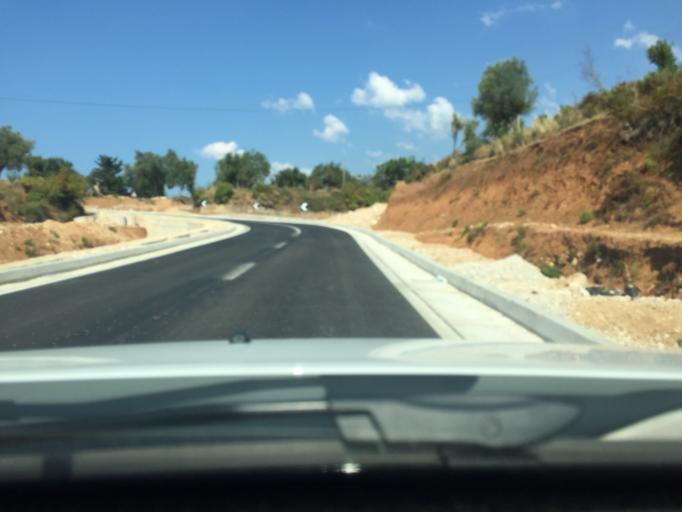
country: AL
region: Vlore
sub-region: Rrethi i Vlores
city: Himare
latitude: 40.1079
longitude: 19.7590
